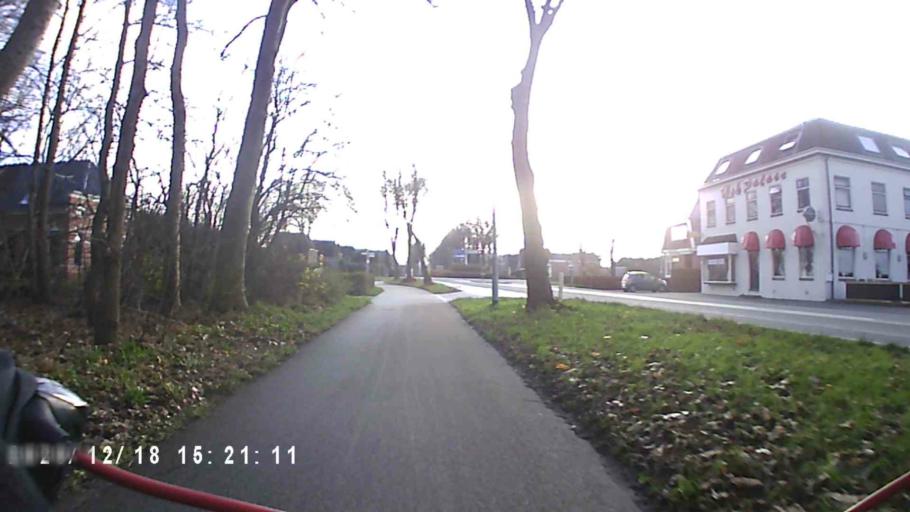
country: NL
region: Groningen
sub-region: Gemeente Hoogezand-Sappemeer
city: Hoogezand
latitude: 53.1528
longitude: 6.7234
